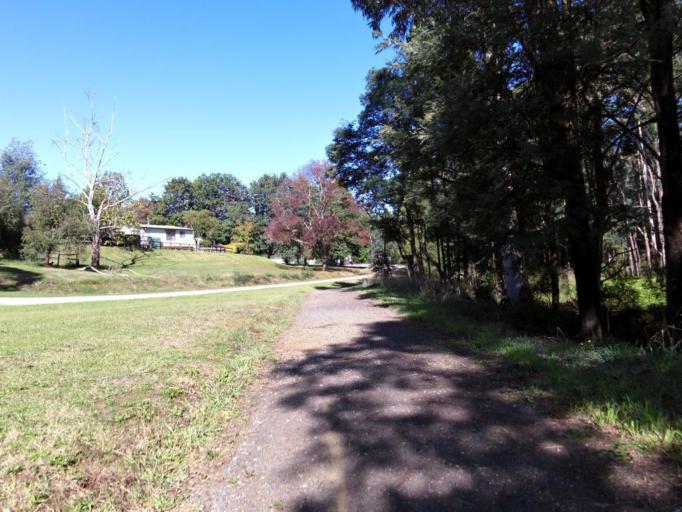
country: AU
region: Victoria
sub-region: Cardinia
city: Cockatoo
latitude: -37.9344
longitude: 145.4904
